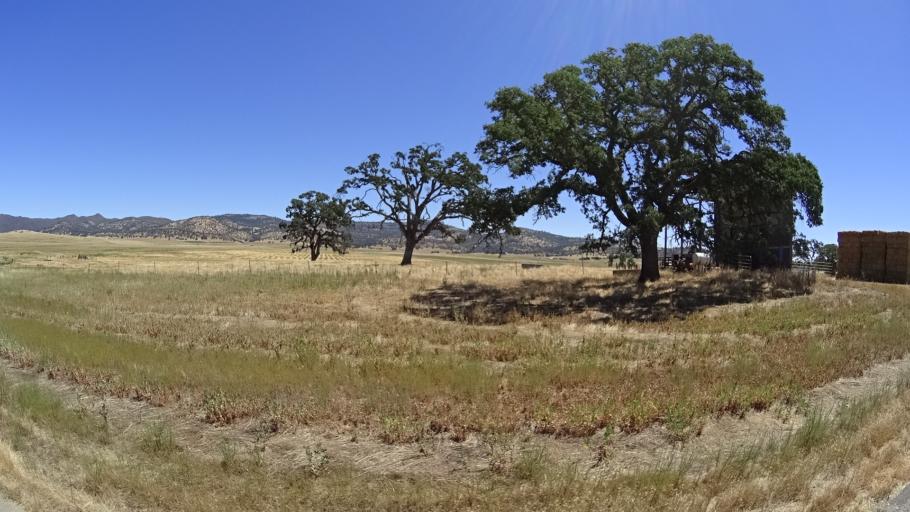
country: US
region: California
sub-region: Calaveras County
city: Copperopolis
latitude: 38.0296
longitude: -120.7176
